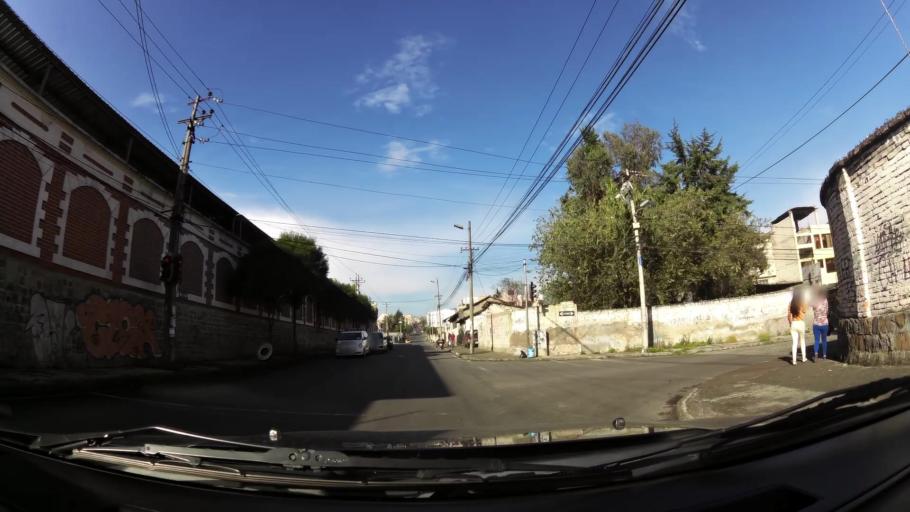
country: EC
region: Pichincha
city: Quito
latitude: -0.2595
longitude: -78.5246
